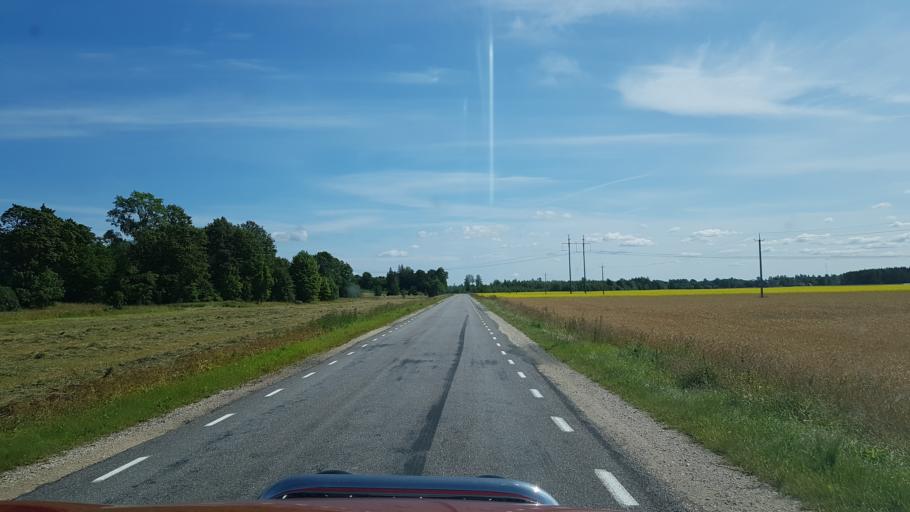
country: EE
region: Laeaene-Virumaa
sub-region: Tapa vald
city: Tapa
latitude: 59.1799
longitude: 25.9185
